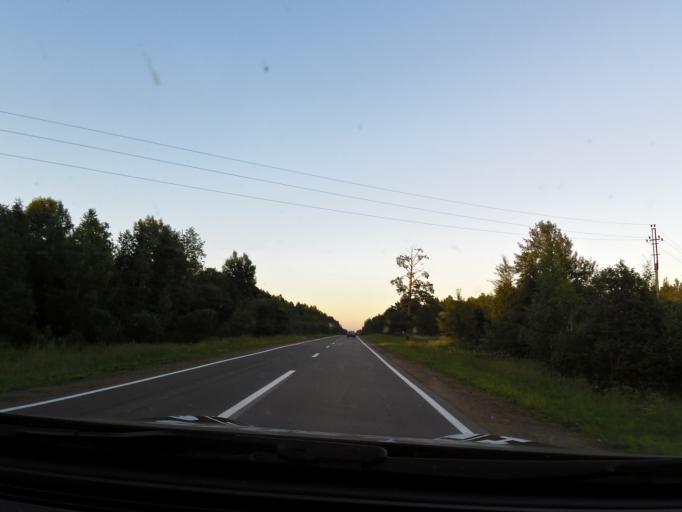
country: RU
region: Jaroslavl
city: Lyubim
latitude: 58.3581
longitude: 40.5619
